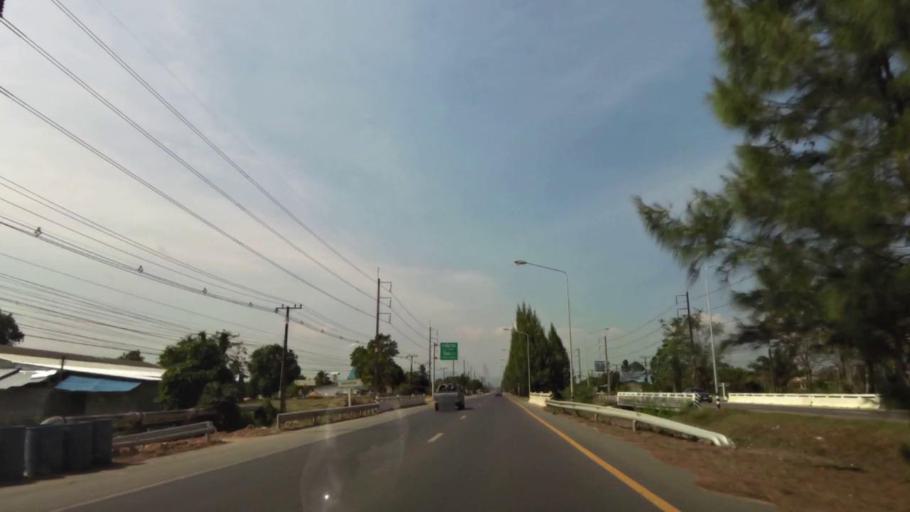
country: TH
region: Chanthaburi
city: Chanthaburi
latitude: 12.6315
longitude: 102.1434
